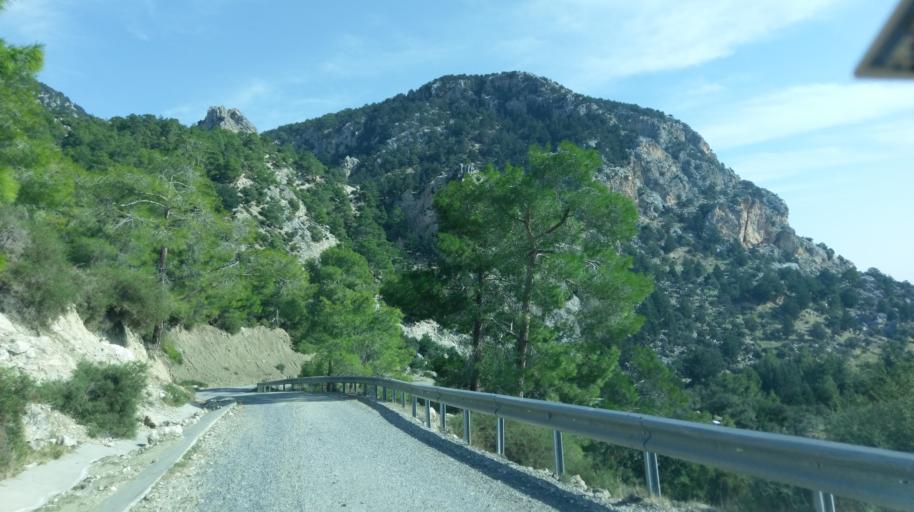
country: CY
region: Keryneia
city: Lapithos
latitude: 35.3212
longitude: 33.1218
